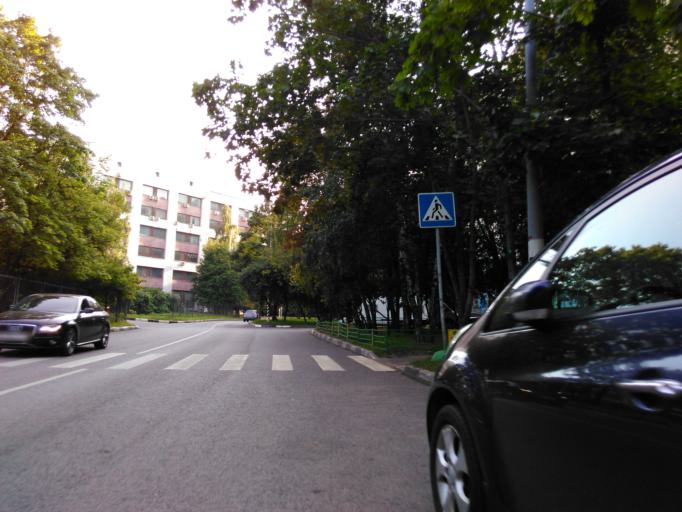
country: RU
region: Moskovskaya
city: Cheremushki
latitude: 55.6504
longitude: 37.5310
